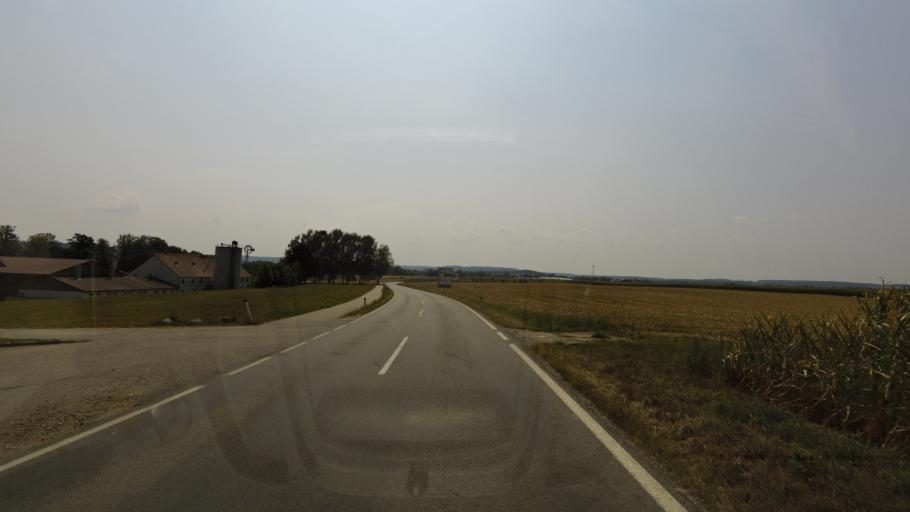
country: DE
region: Bavaria
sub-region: Lower Bavaria
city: Bad Fussing
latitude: 48.3066
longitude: 13.3292
